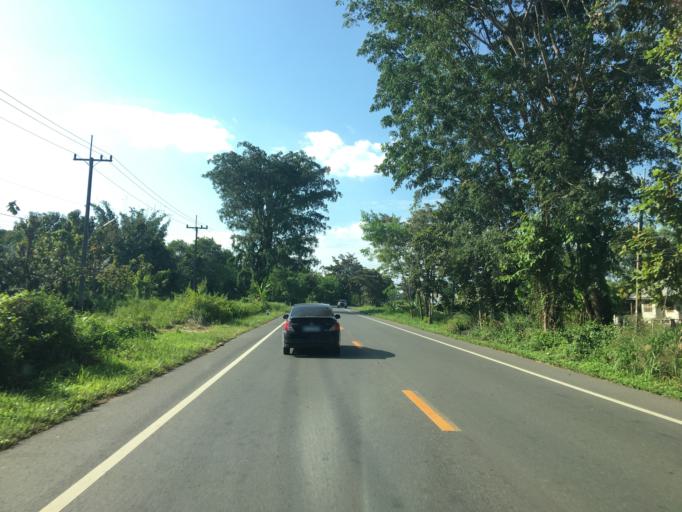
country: TH
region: Phayao
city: Chun
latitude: 19.3542
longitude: 100.1003
